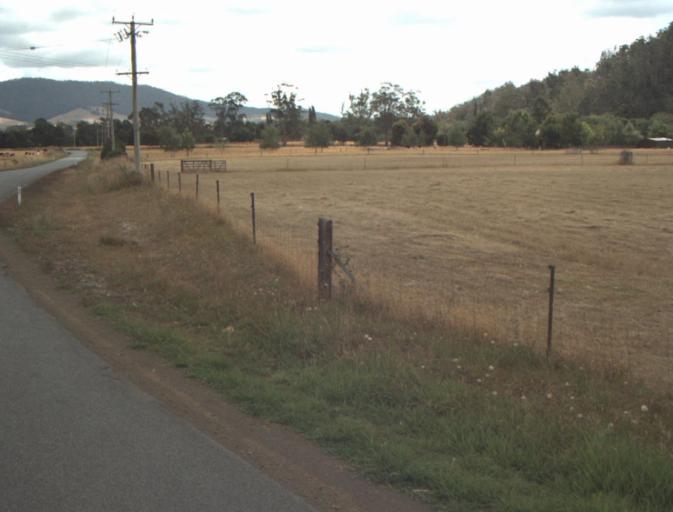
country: AU
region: Tasmania
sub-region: Launceston
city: Mayfield
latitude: -41.2394
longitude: 147.1756
